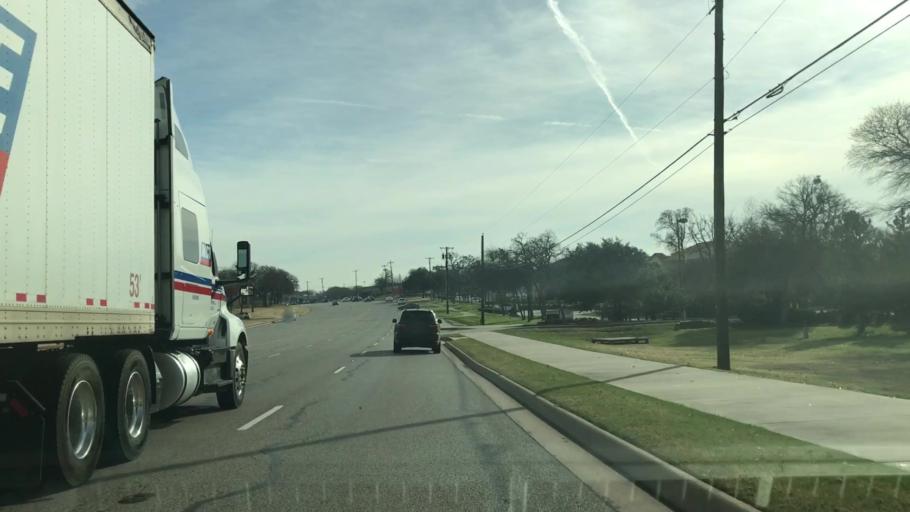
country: US
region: Texas
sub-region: Tarrant County
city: Southlake
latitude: 32.9389
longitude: -97.1099
